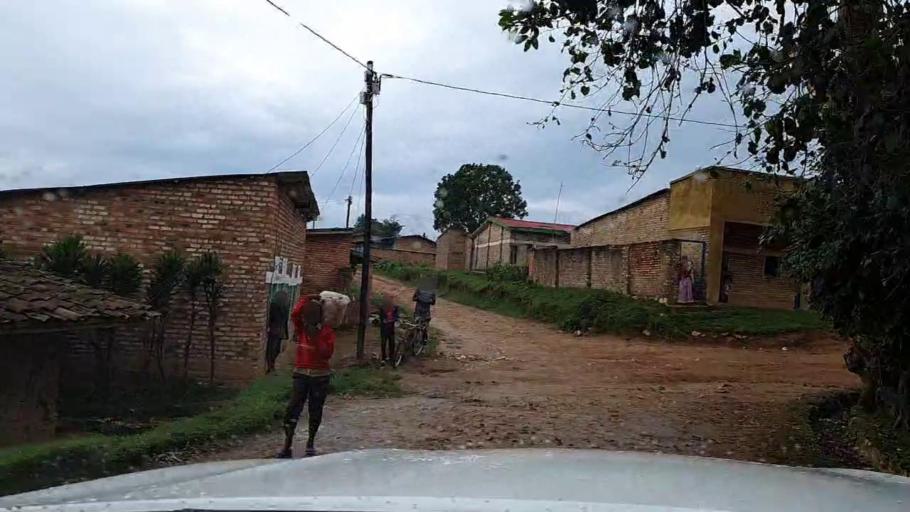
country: RW
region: Southern Province
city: Nzega
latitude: -2.4580
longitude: 29.4670
